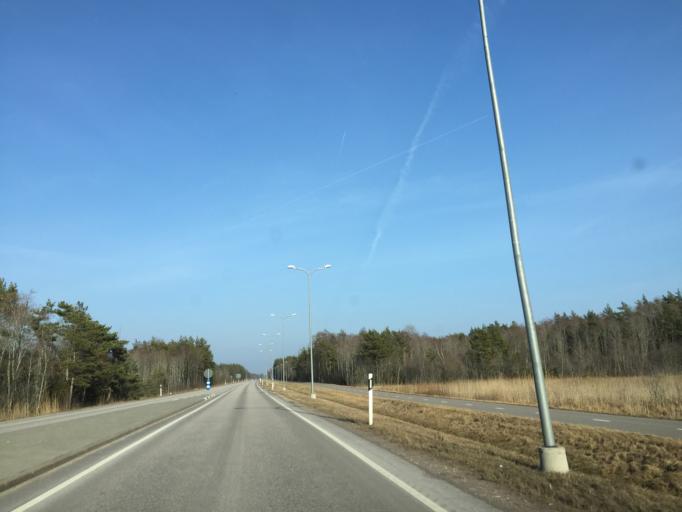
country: EE
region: Saare
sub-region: Kuressaare linn
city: Kuressaare
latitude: 58.2319
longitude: 22.4157
